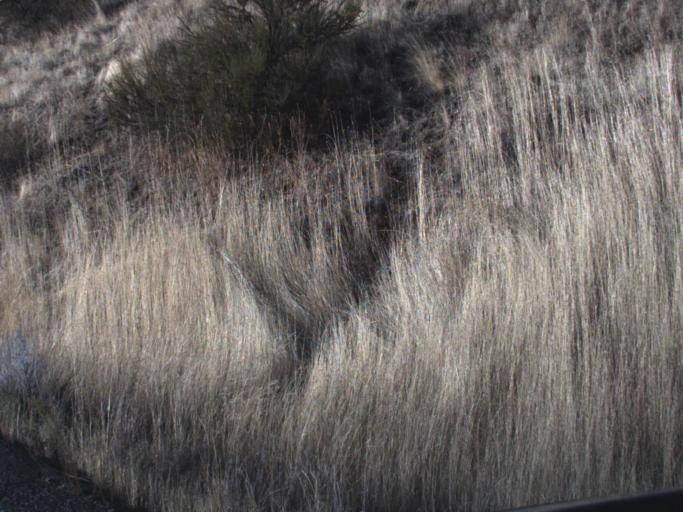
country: US
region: Washington
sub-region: Okanogan County
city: Coulee Dam
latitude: 47.9854
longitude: -118.6934
